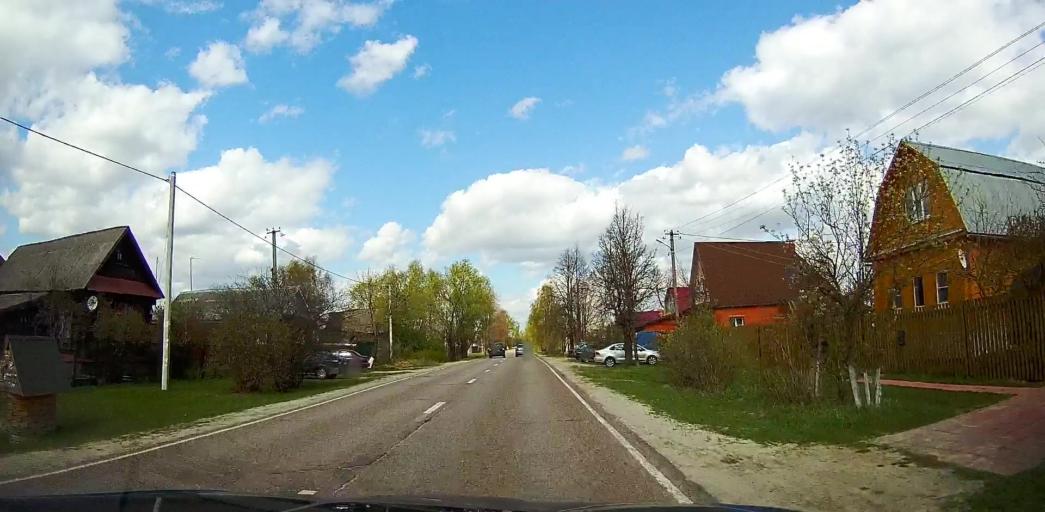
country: RU
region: Moskovskaya
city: Davydovo
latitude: 55.5778
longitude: 38.8225
